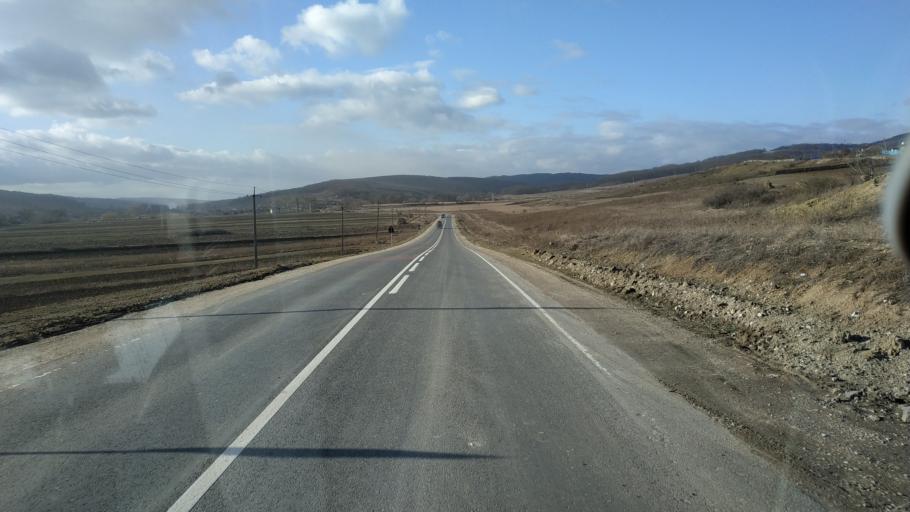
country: MD
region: Calarasi
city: Calarasi
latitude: 47.3232
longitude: 28.1058
